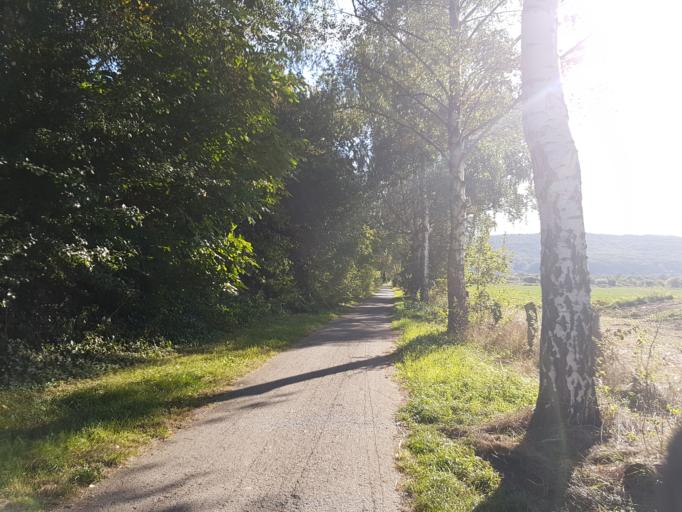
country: DE
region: North Rhine-Westphalia
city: Porta Westfalica
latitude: 52.2626
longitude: 8.9257
